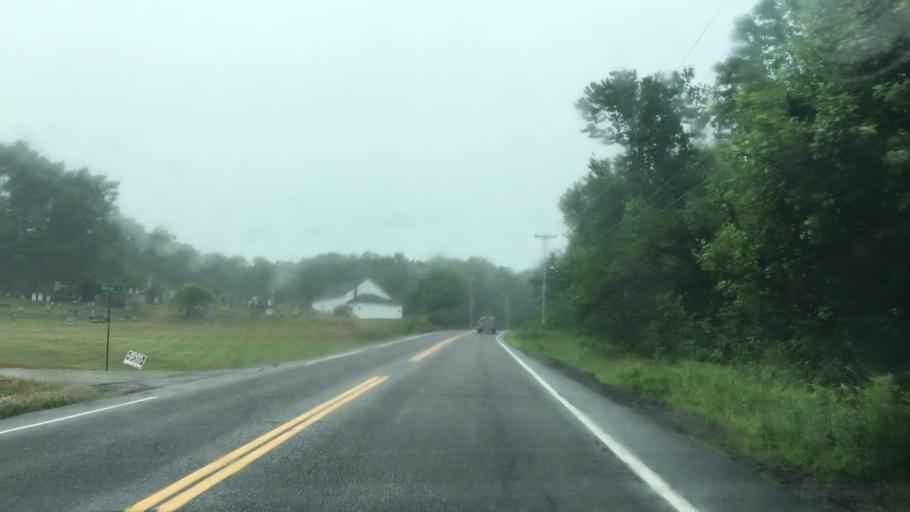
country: US
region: Maine
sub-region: Lincoln County
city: Edgecomb
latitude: 43.9767
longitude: -69.6355
